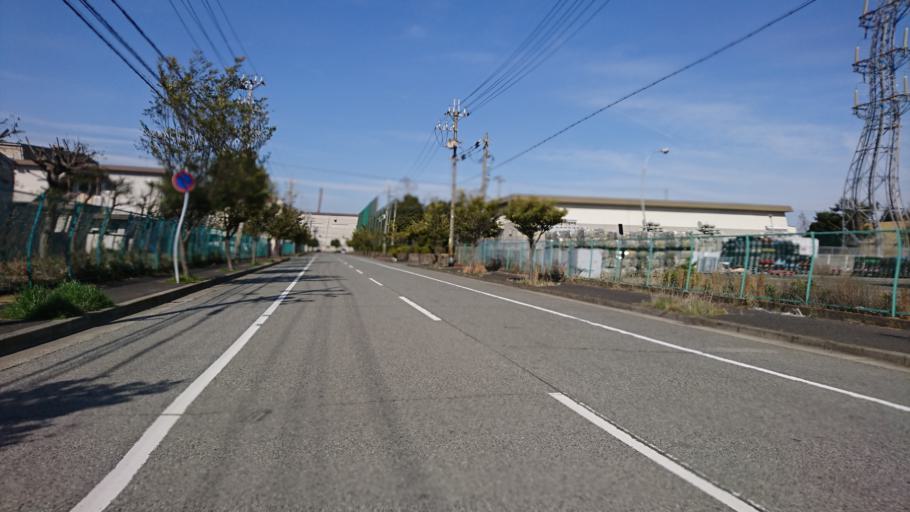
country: JP
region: Hyogo
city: Kakogawacho-honmachi
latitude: 34.7008
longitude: 134.8495
